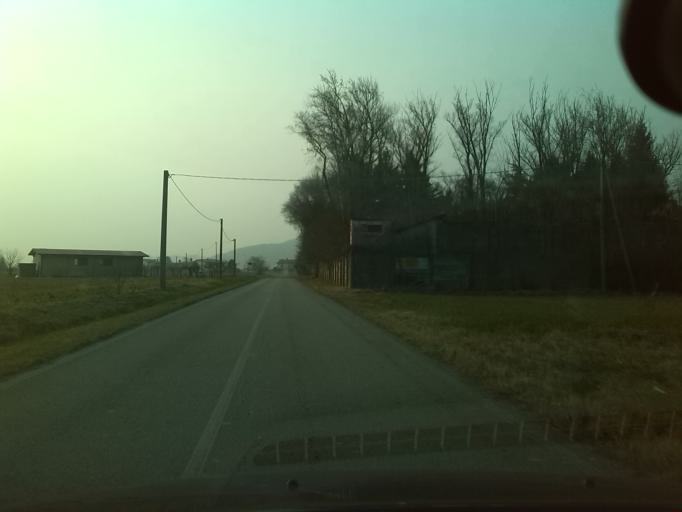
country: IT
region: Friuli Venezia Giulia
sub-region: Provincia di Udine
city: San Pietro al Natisone
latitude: 46.0987
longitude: 13.4685
